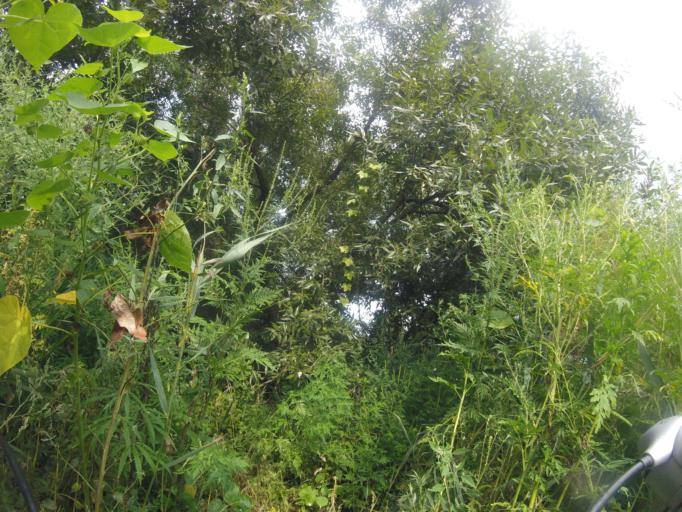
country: HU
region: Somogy
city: Adand
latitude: 46.8733
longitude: 18.1871
